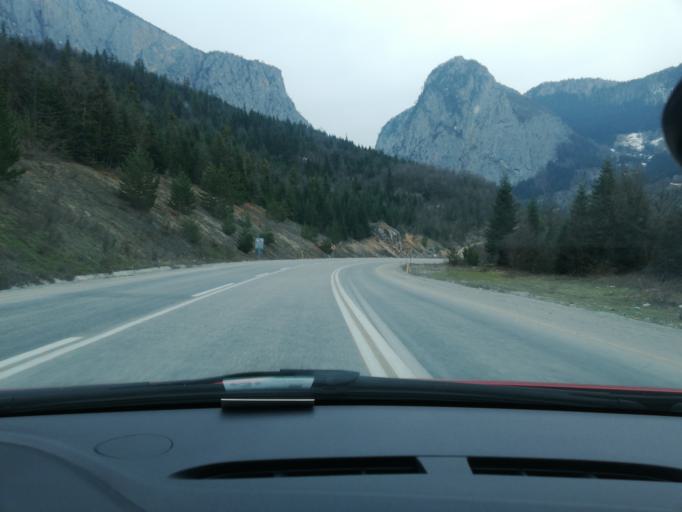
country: TR
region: Kastamonu
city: Kure
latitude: 41.8455
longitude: 33.7243
